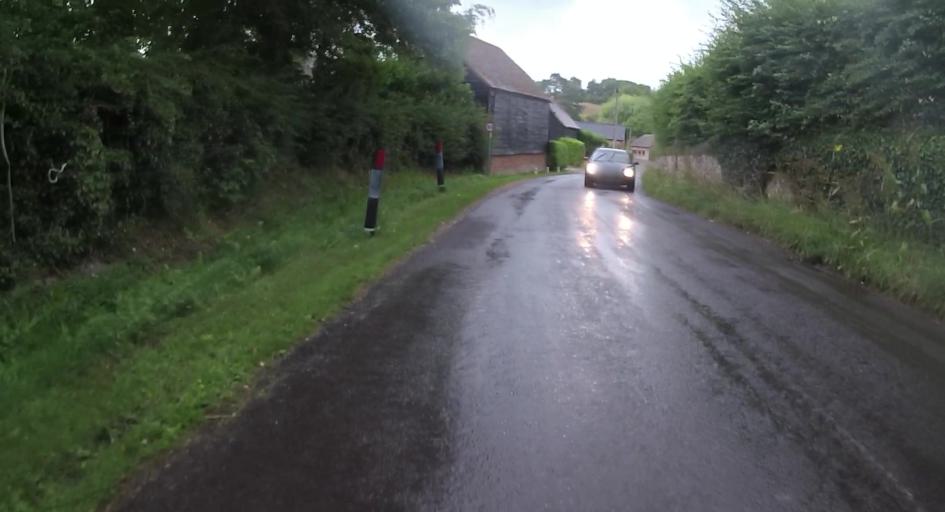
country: GB
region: England
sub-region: Hampshire
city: Long Sutton
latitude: 51.1822
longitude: -0.9185
